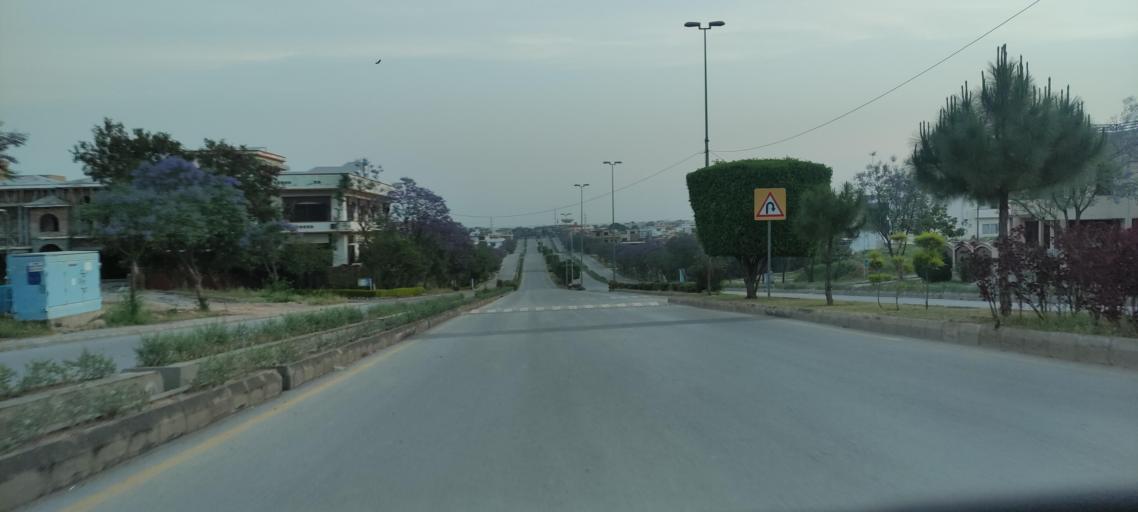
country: PK
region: Punjab
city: Rawalpindi
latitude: 33.5221
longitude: 73.1651
